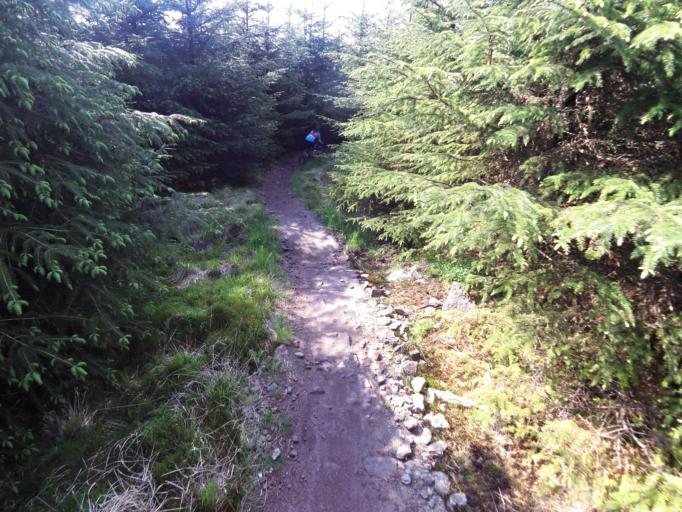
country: GB
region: England
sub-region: North Yorkshire
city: Settle
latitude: 54.0221
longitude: -2.3741
